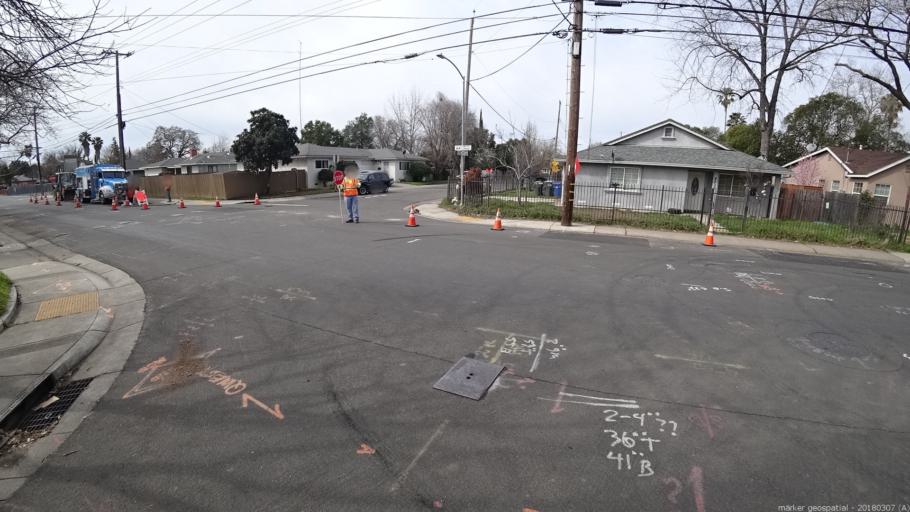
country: US
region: California
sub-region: Sacramento County
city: Parkway
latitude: 38.5359
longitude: -121.4554
